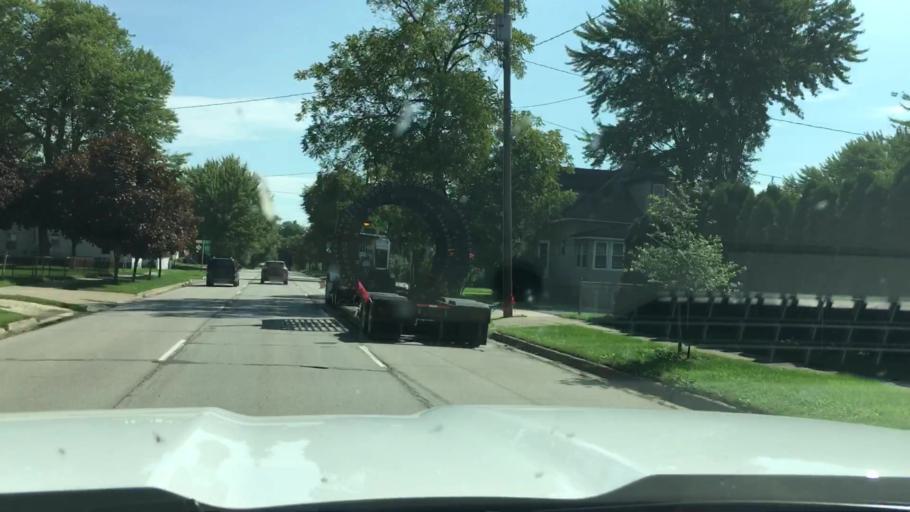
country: US
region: Michigan
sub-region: Bay County
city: Bay City
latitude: 43.5974
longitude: -83.9119
